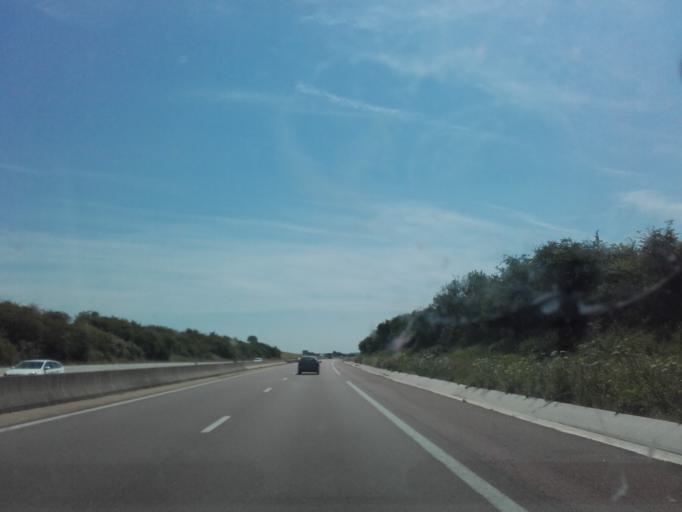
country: FR
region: Bourgogne
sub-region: Departement de l'Yonne
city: Avallon
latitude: 47.5036
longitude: 4.0969
